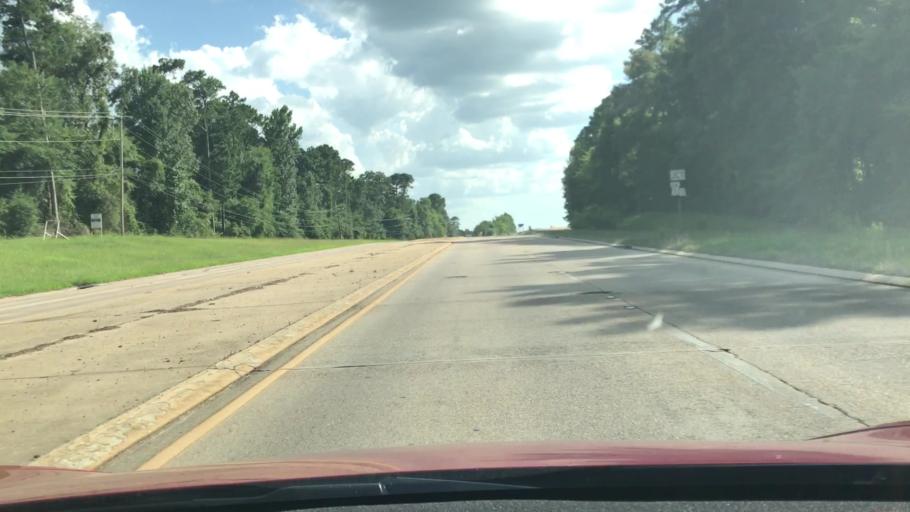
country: US
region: Louisiana
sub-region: Bossier Parish
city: Bossier City
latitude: 32.4048
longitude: -93.7307
